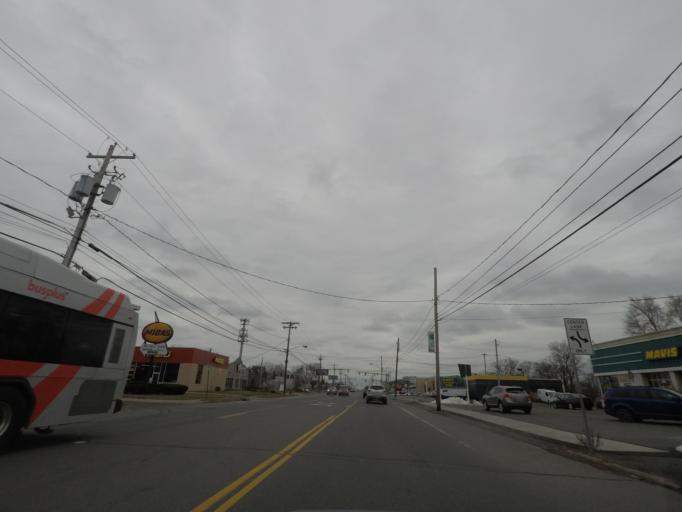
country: US
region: New York
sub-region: Schenectady County
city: Schenectady
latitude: 42.7866
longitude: -73.9112
